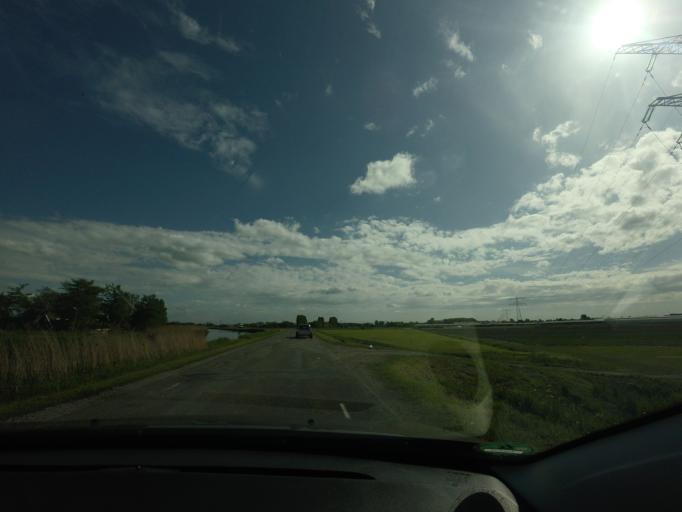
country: NL
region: North Holland
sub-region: Gemeente Heerhugowaard
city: Heerhugowaard
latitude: 52.6538
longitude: 4.8625
